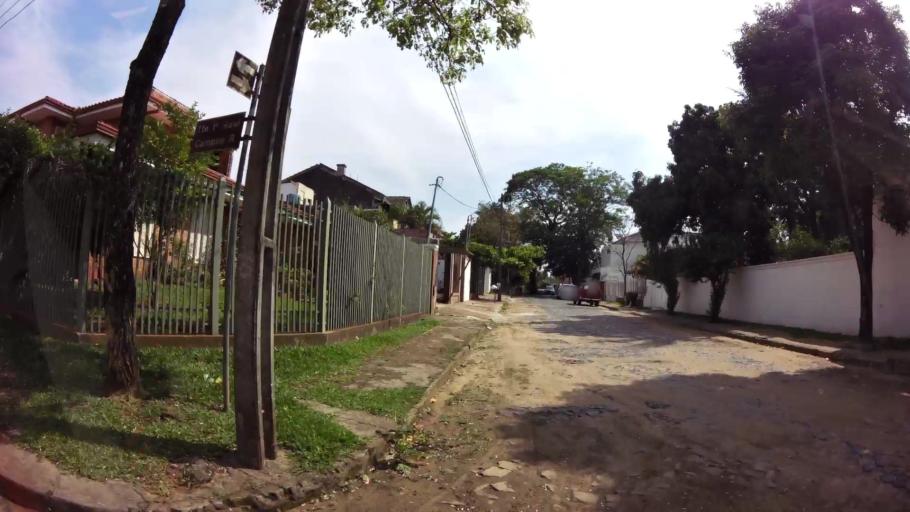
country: PY
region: Asuncion
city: Asuncion
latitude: -25.2648
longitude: -57.5623
